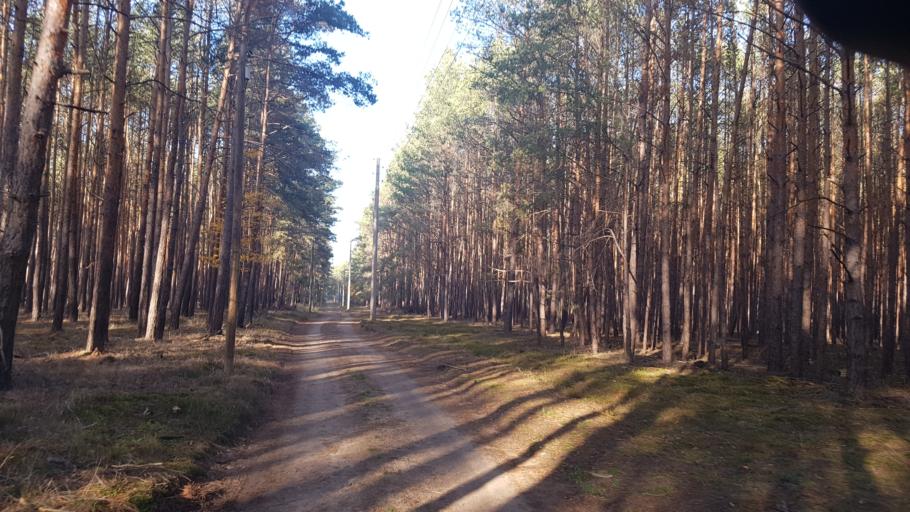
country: DE
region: Brandenburg
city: Schilda
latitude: 51.6419
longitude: 13.3508
